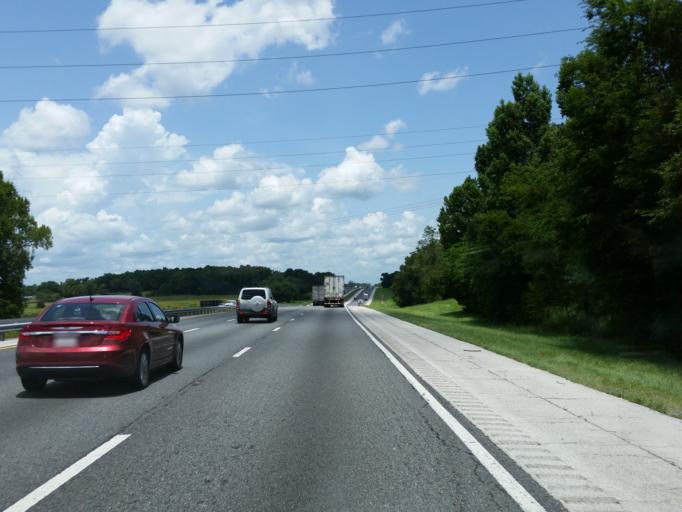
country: US
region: Florida
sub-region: Marion County
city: Ocala
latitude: 29.3023
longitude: -82.2058
